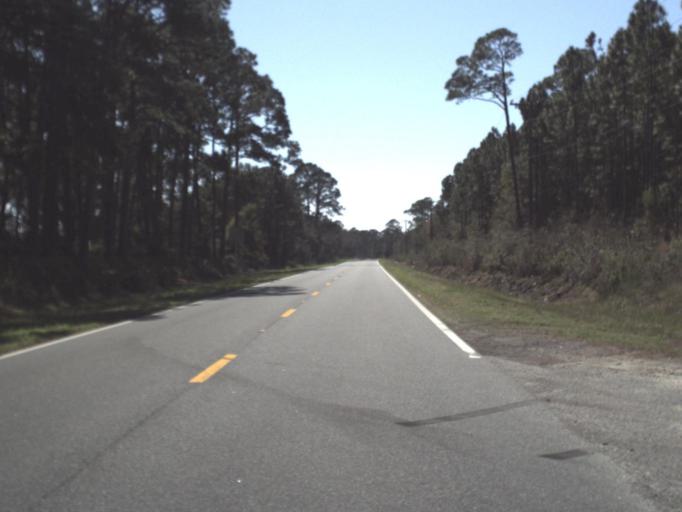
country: US
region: Florida
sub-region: Franklin County
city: Carrabelle
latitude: 29.8675
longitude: -84.6158
